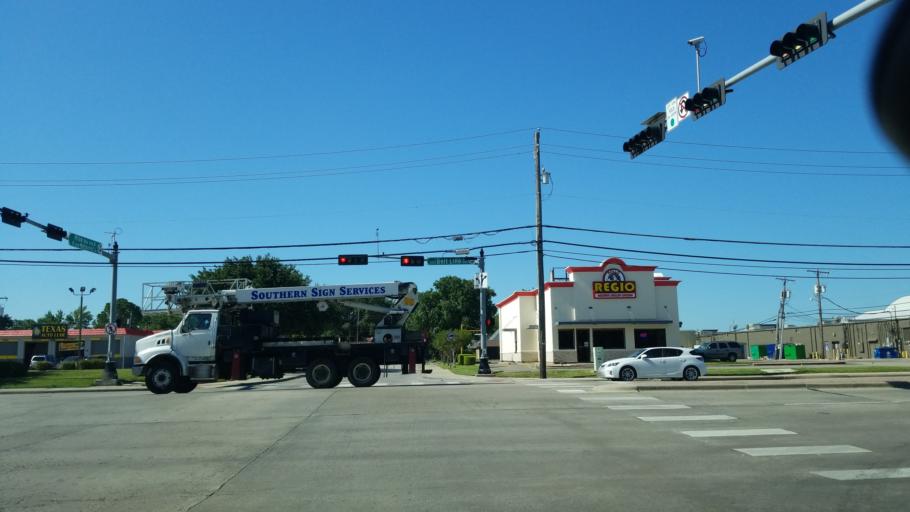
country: US
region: Texas
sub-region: Dallas County
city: Carrollton
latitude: 32.9538
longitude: -96.8870
